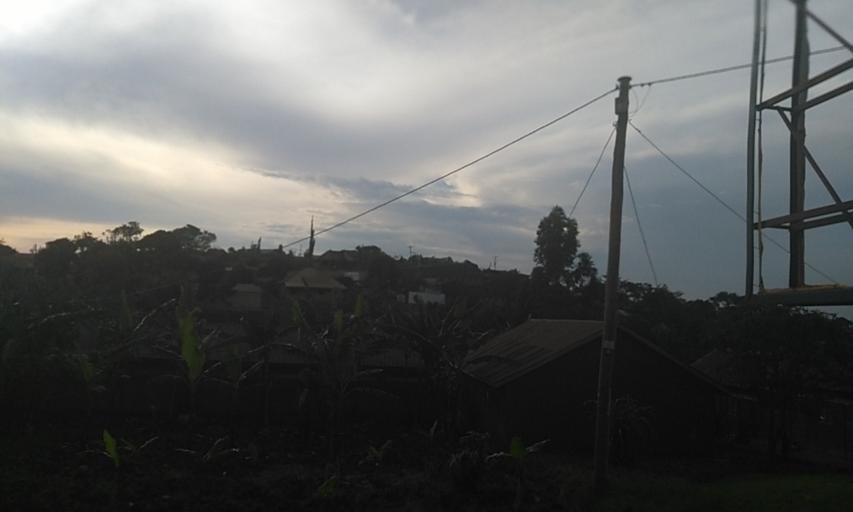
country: UG
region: Central Region
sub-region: Wakiso District
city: Kajansi
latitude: 0.2646
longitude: 32.5123
